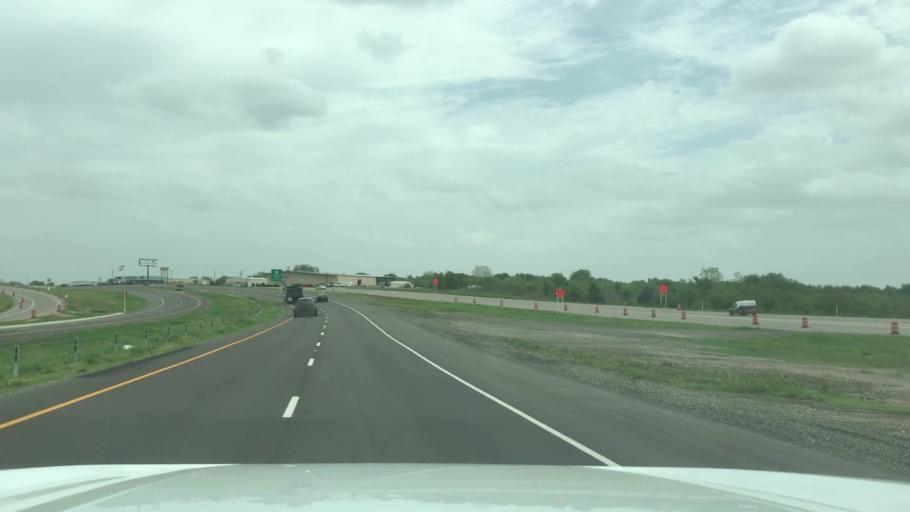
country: US
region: Texas
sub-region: McLennan County
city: Beverly Hills
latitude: 31.4915
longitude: -97.1473
